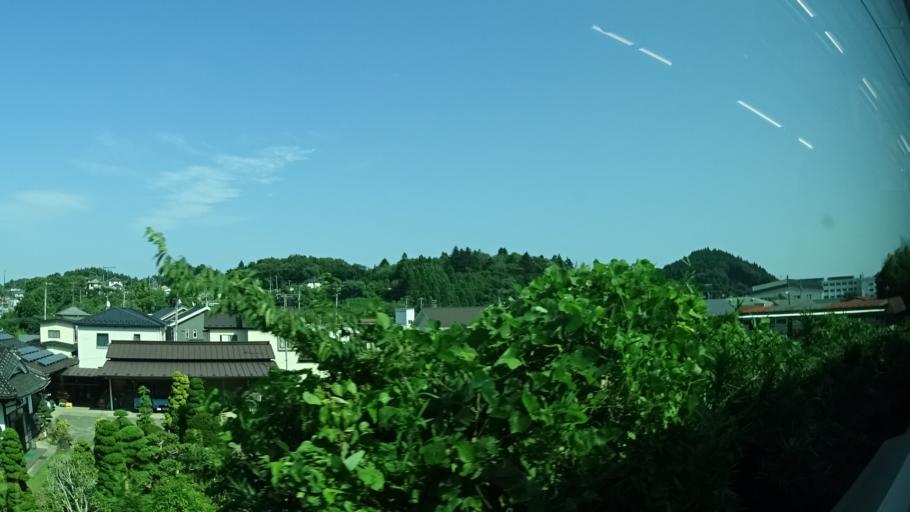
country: JP
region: Miyagi
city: Matsushima
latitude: 38.3995
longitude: 141.0659
